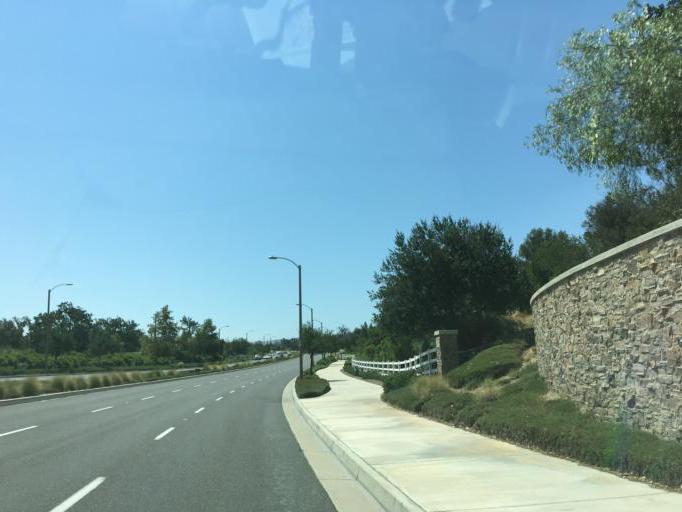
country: US
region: California
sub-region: Los Angeles County
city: Santa Clarita
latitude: 34.4030
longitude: -118.5768
